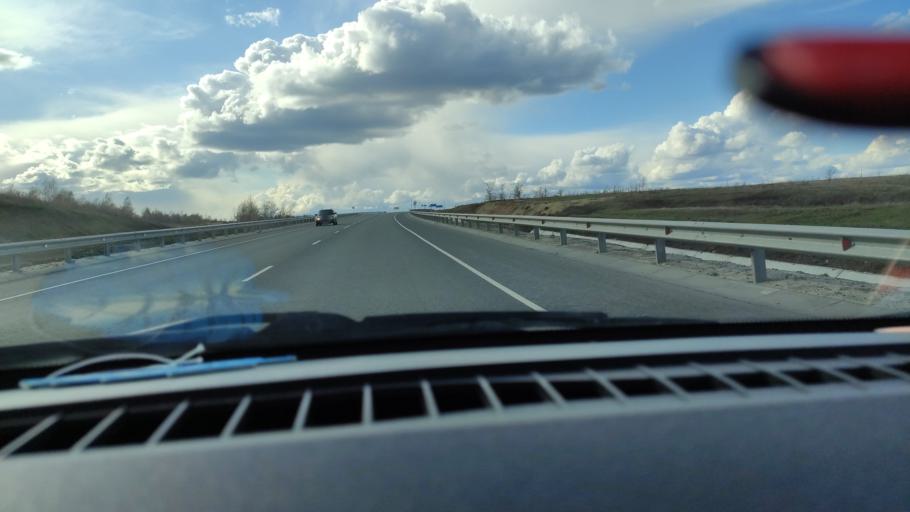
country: RU
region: Saratov
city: Shikhany
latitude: 52.1294
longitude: 47.2329
